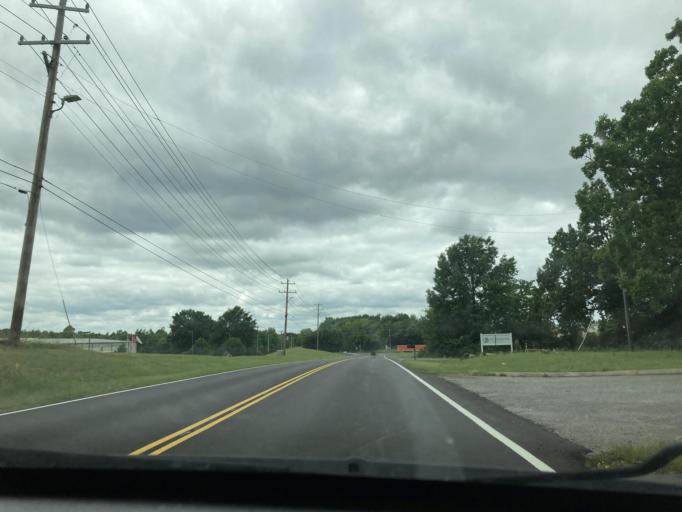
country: US
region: Tennessee
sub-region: Dickson County
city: Burns
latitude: 36.0541
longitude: -87.3487
